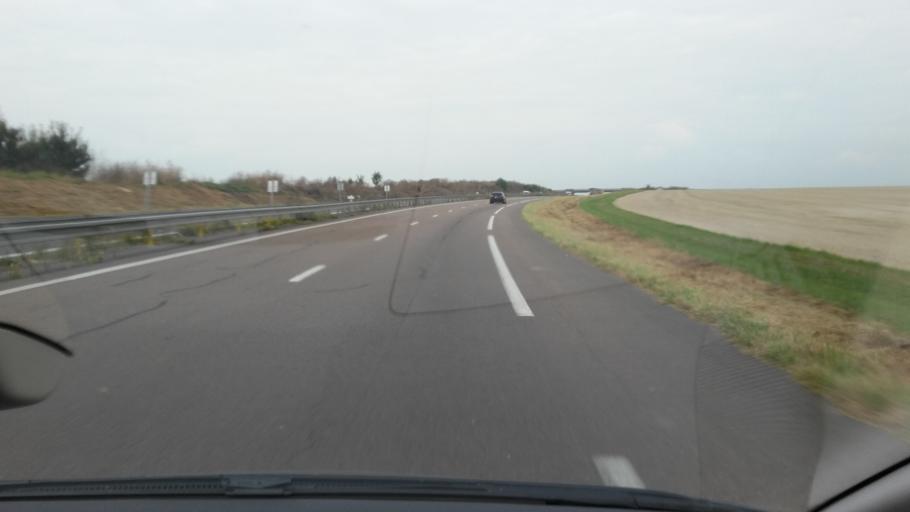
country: FR
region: Champagne-Ardenne
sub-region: Departement de la Marne
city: Warmeriville
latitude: 49.3631
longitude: 4.2087
